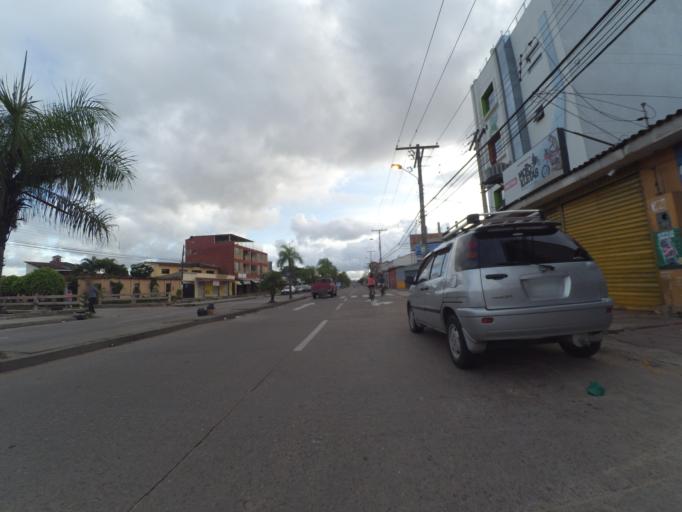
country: BO
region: Santa Cruz
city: Santa Cruz de la Sierra
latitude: -17.7579
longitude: -63.1560
